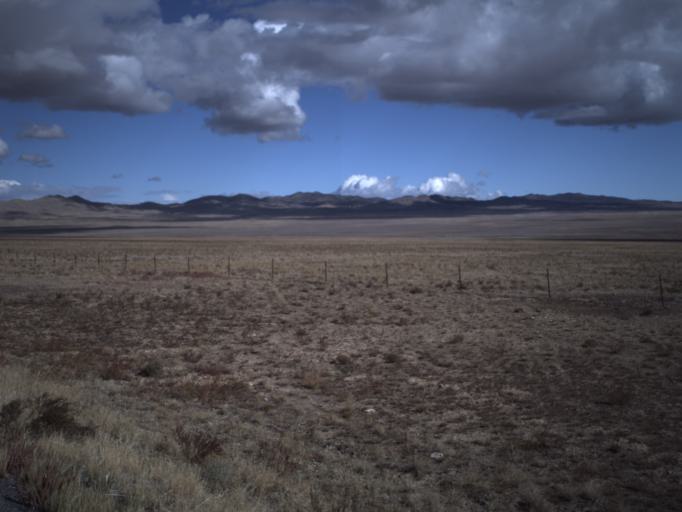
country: US
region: Utah
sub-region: Beaver County
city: Milford
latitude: 38.6728
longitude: -113.8863
